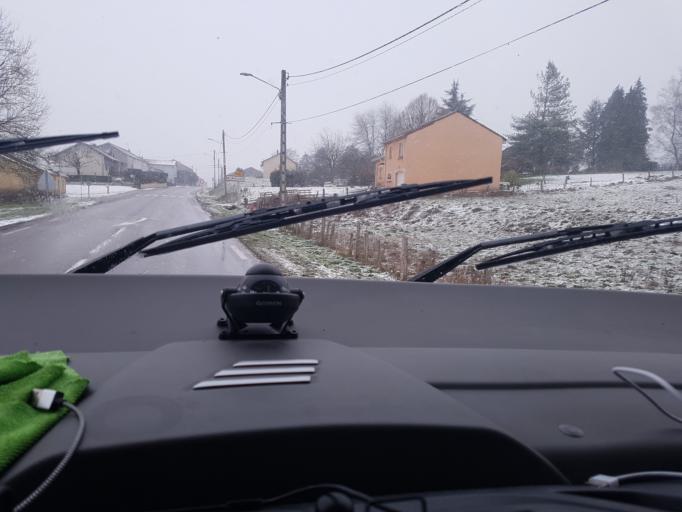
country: FR
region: Lorraine
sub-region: Departement de Meurthe-et-Moselle
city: Baccarat
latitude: 48.4833
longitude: 6.7798
